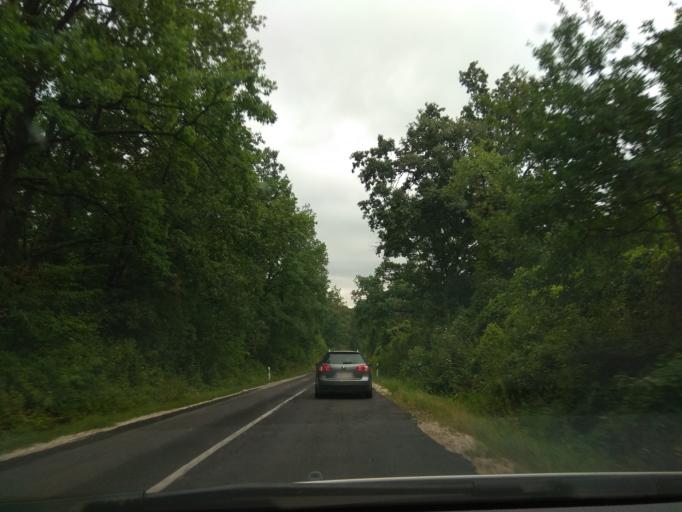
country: HU
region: Borsod-Abauj-Zemplen
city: Harsany
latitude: 48.0194
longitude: 20.7637
